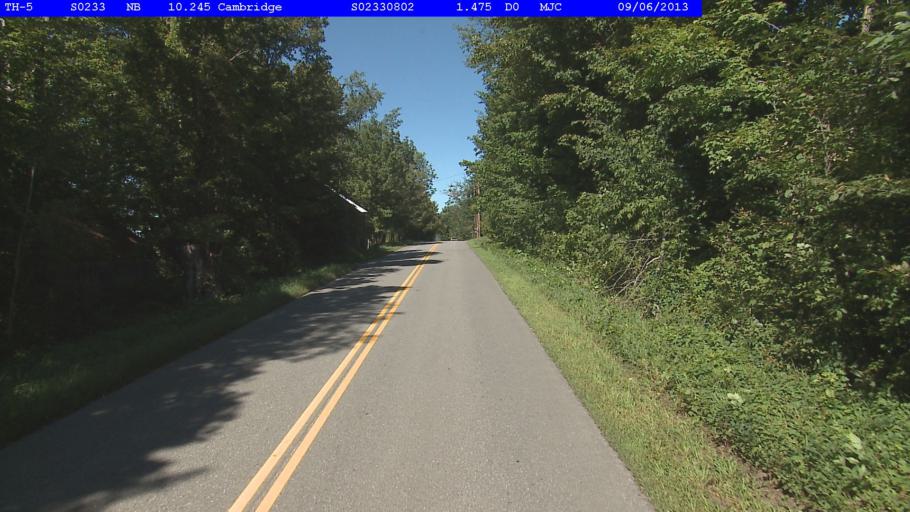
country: US
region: Vermont
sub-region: Chittenden County
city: Jericho
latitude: 44.6030
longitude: -72.8569
